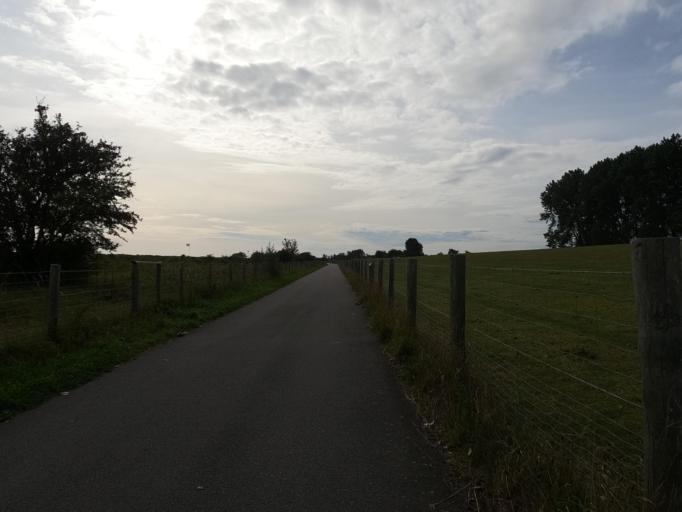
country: DE
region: Schleswig-Holstein
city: Dahme
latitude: 54.2480
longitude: 11.0803
